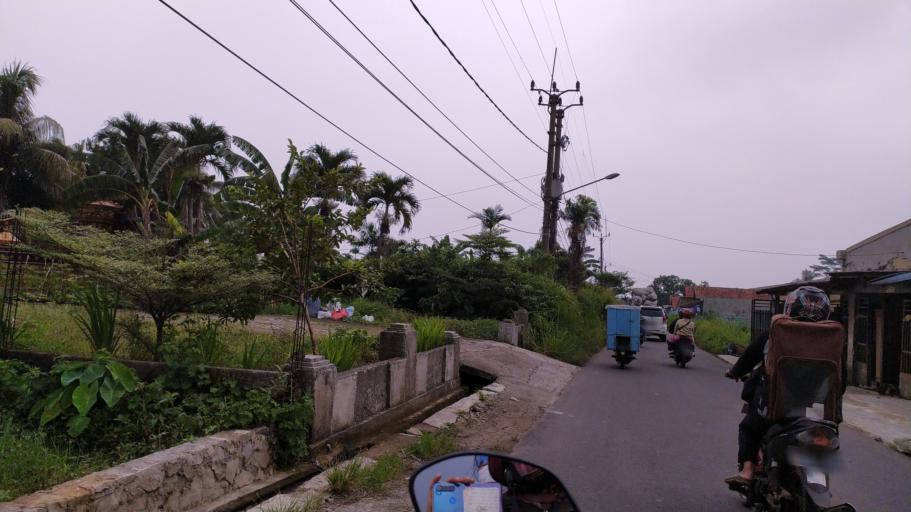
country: ID
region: West Java
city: Ciampea
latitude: -6.6006
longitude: 106.7030
